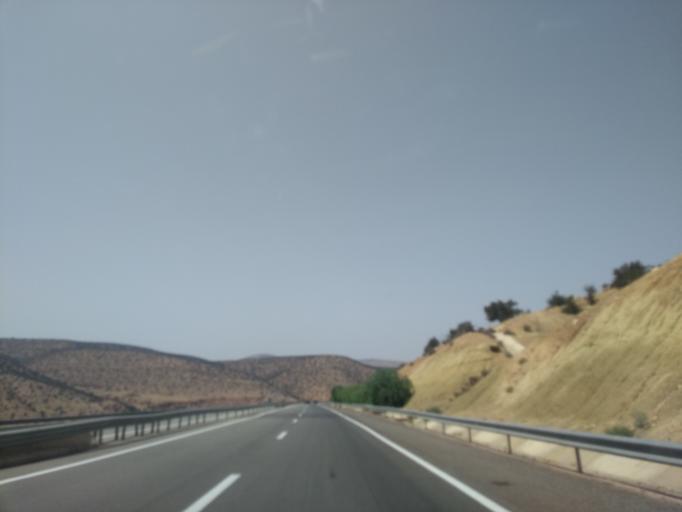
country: MA
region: Marrakech-Tensift-Al Haouz
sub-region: Chichaoua
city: Taouloukoult
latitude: 31.1202
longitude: -9.0162
